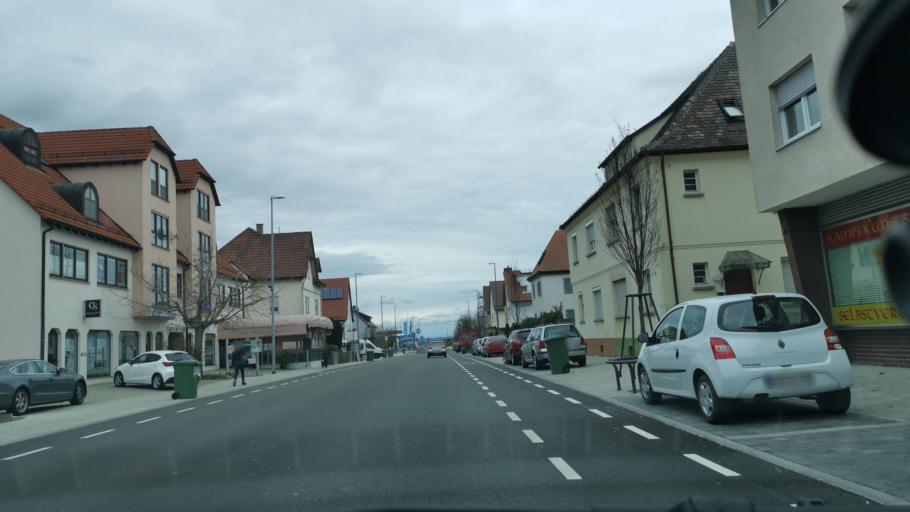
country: DE
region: Baden-Wuerttemberg
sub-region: Regierungsbezirk Stuttgart
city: Markgroningen
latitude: 48.9050
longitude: 9.0878
